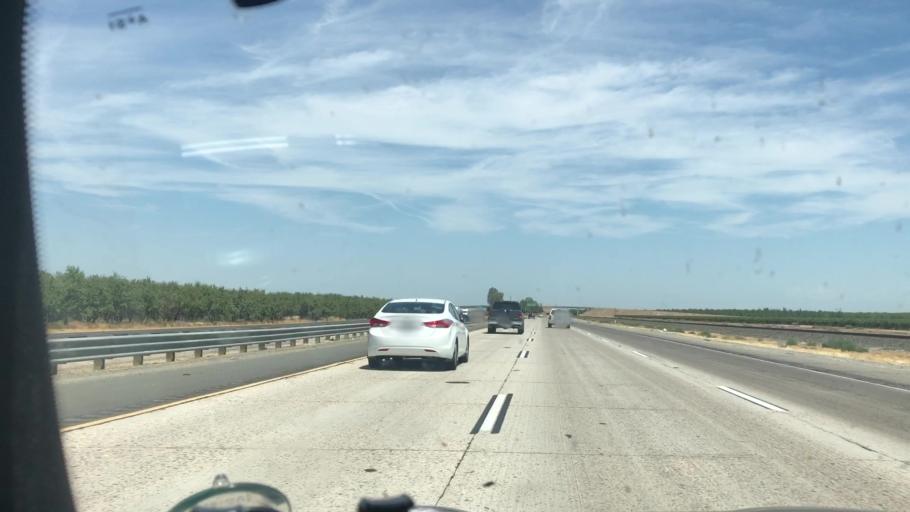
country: US
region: California
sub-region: Kern County
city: McFarland
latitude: 35.6377
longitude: -119.2176
